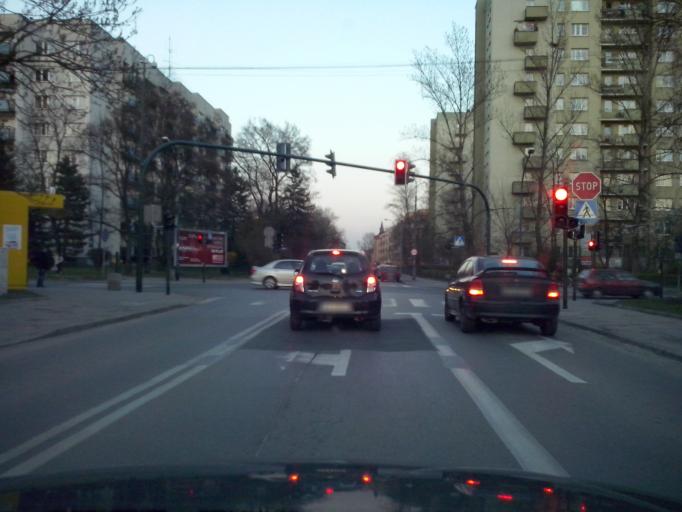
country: PL
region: Lesser Poland Voivodeship
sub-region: Krakow
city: Krakow
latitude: 50.0725
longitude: 19.9044
